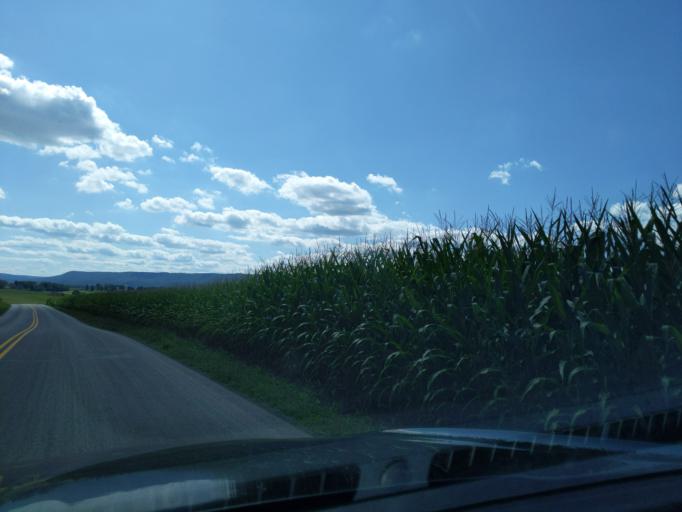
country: US
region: Pennsylvania
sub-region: Blair County
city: Tyrone
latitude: 40.6331
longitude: -78.2260
